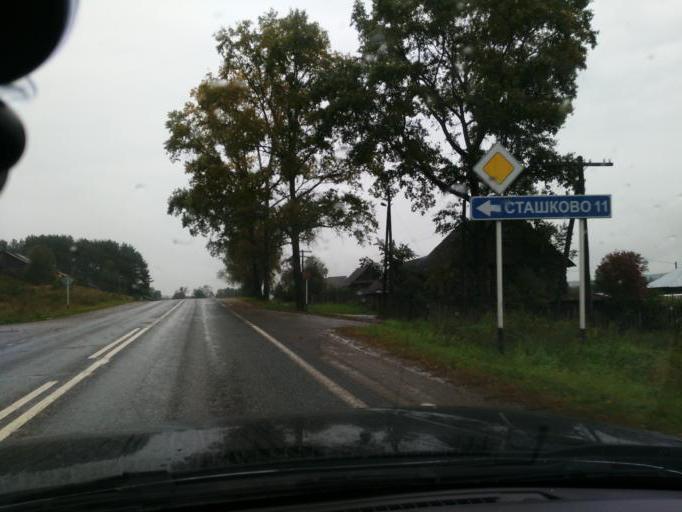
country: RU
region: Perm
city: Yugo-Kamskiy
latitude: 57.5497
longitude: 55.6850
